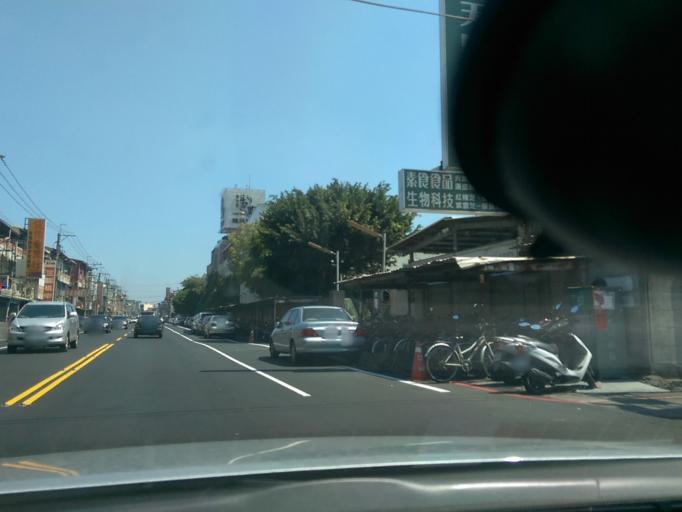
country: TW
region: Taiwan
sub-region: Chiayi
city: Jiayi Shi
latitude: 23.4462
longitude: 120.4576
